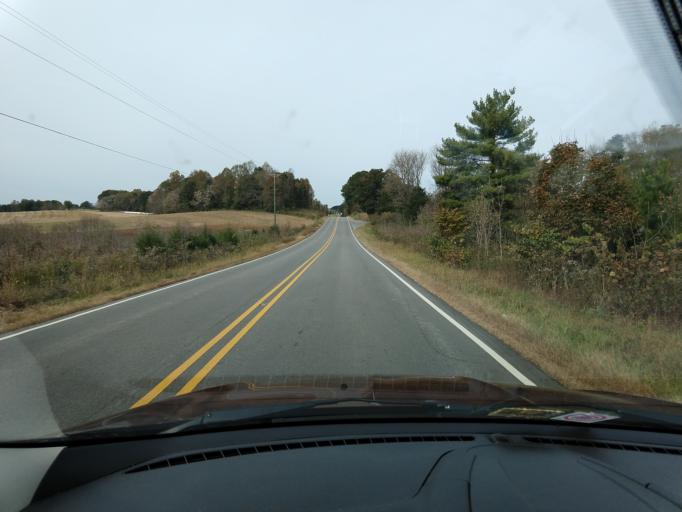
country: US
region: Virginia
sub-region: Franklin County
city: Union Hall
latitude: 36.9599
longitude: -79.5713
